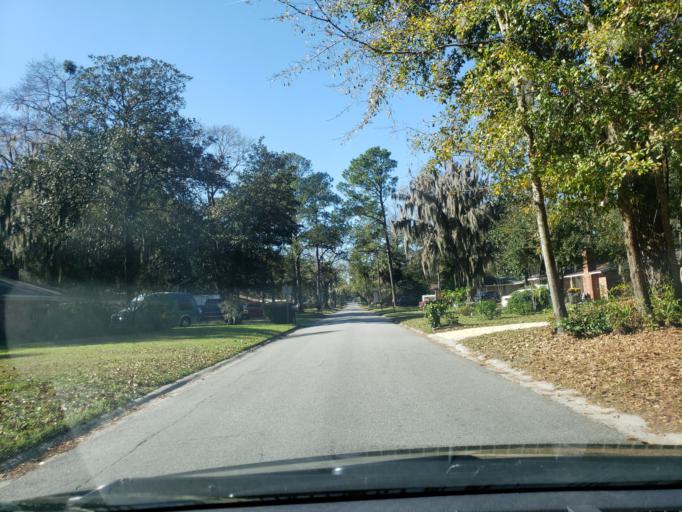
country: US
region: Georgia
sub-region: Chatham County
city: Montgomery
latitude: 31.9712
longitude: -81.1391
